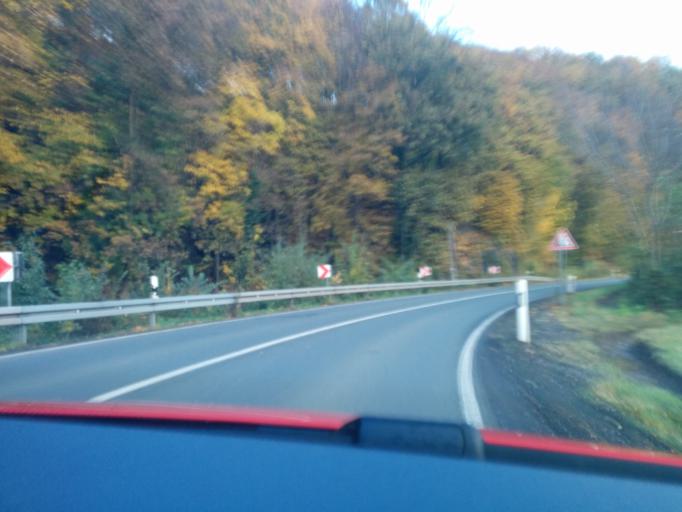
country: DE
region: Saxony
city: Dohna
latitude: 50.9397
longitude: 13.8582
